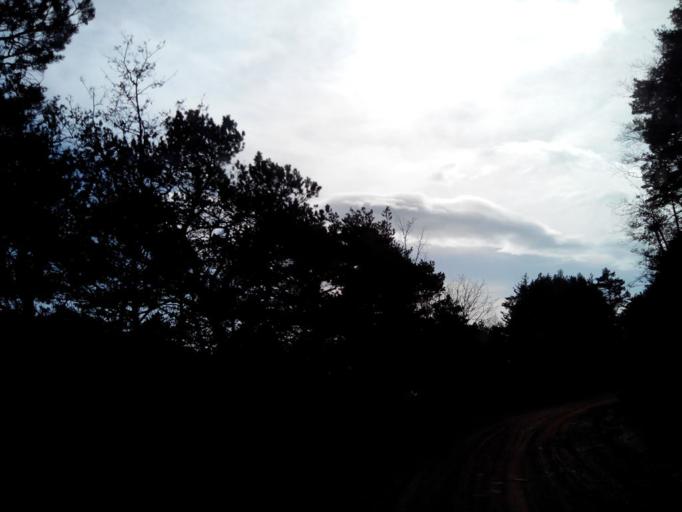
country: ES
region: Catalonia
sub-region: Provincia de Barcelona
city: Vilada
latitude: 42.1640
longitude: 1.9311
